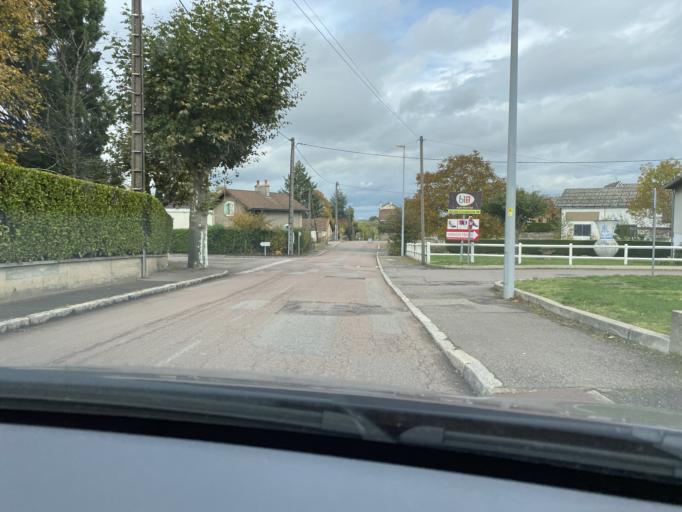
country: FR
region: Bourgogne
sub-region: Departement de la Cote-d'Or
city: Saulieu
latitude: 47.2817
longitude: 4.2363
